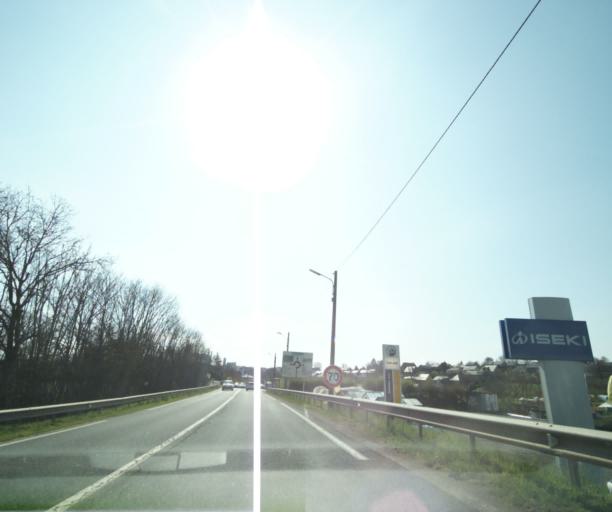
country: FR
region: Midi-Pyrenees
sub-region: Departement de l'Aveyron
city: Olemps
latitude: 44.3660
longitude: 2.5503
